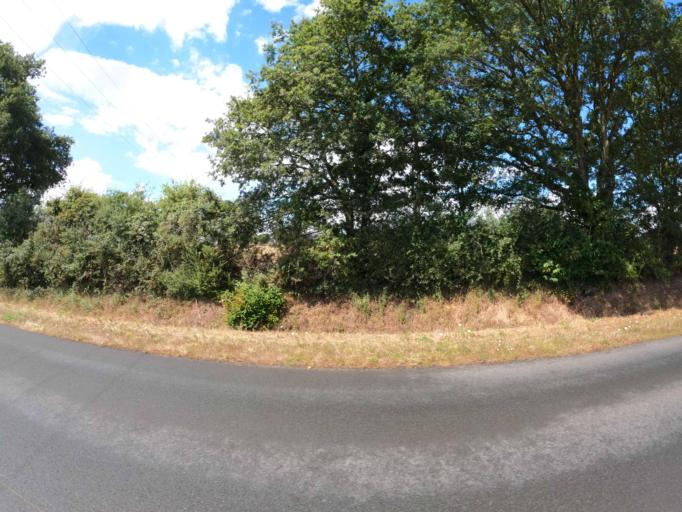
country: FR
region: Pays de la Loire
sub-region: Departement de Maine-et-Loire
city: Feneu
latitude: 47.5913
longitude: -0.5896
